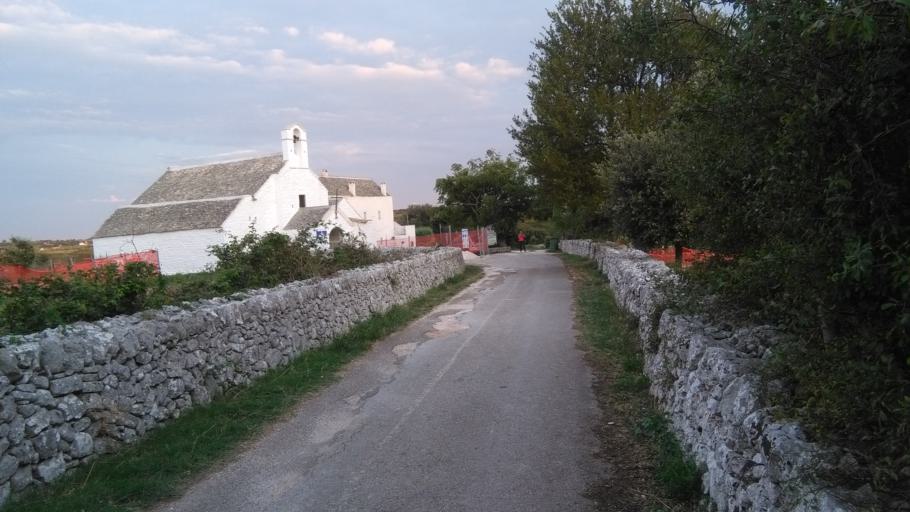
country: IT
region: Apulia
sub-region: Provincia di Bari
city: Alberobello
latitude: 40.8070
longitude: 17.1938
